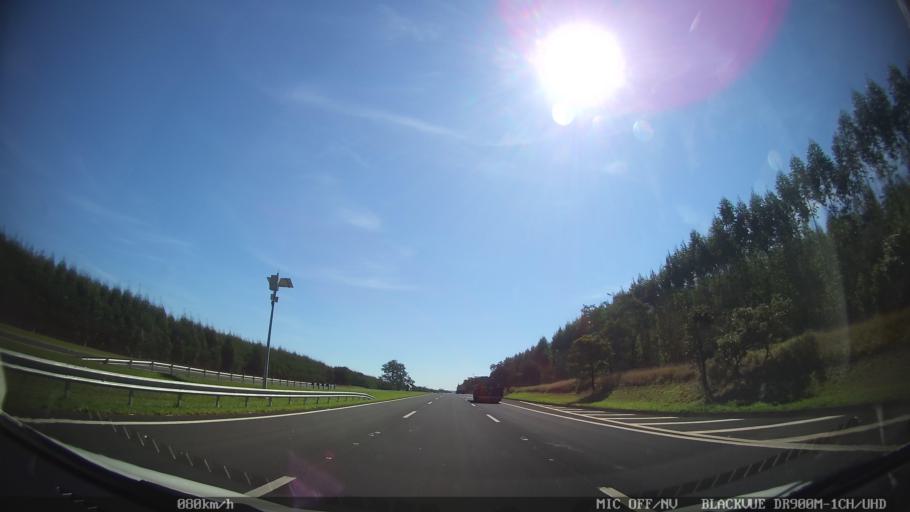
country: BR
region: Sao Paulo
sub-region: Sao Simao
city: Sao Simao
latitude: -21.5644
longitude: -47.6334
